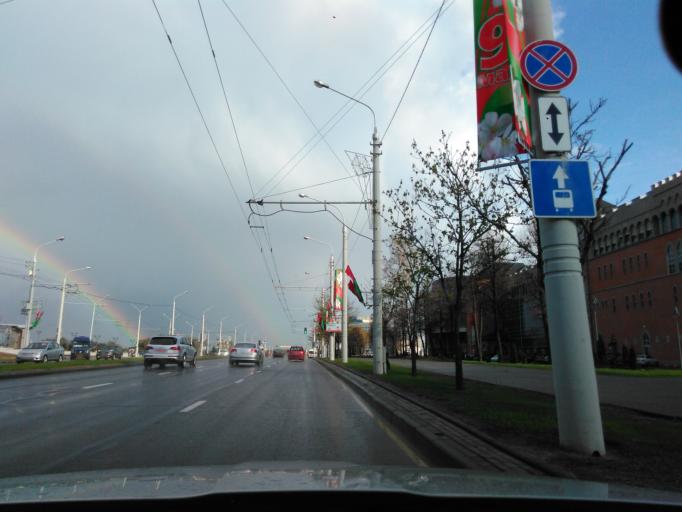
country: BY
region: Minsk
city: Minsk
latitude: 53.9278
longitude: 27.5170
